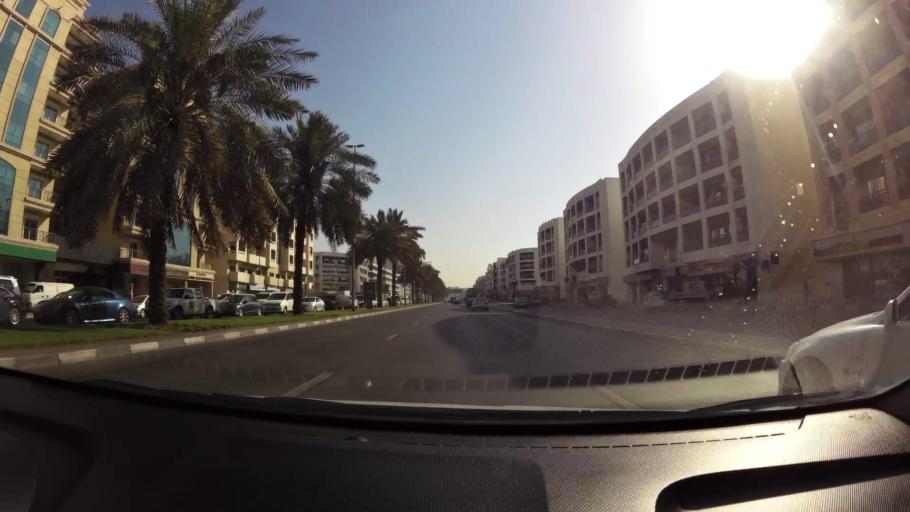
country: AE
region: Ash Shariqah
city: Sharjah
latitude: 25.2873
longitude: 55.3915
